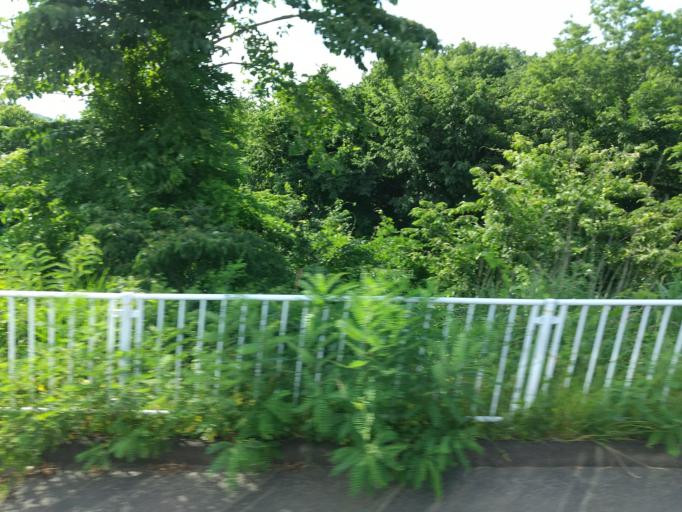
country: JP
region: Miyagi
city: Sendai
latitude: 38.2404
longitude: 140.7326
